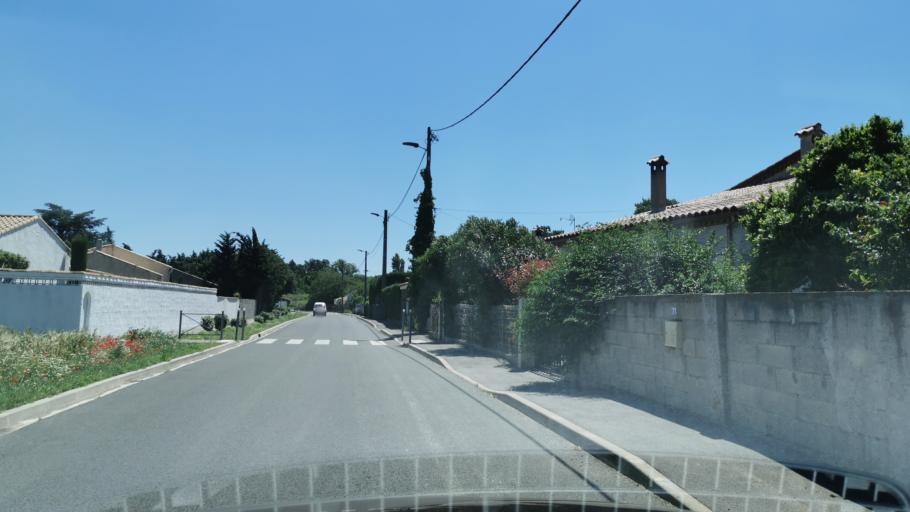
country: FR
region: Languedoc-Roussillon
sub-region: Departement de l'Aude
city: Moussan
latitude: 43.2455
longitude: 2.9872
